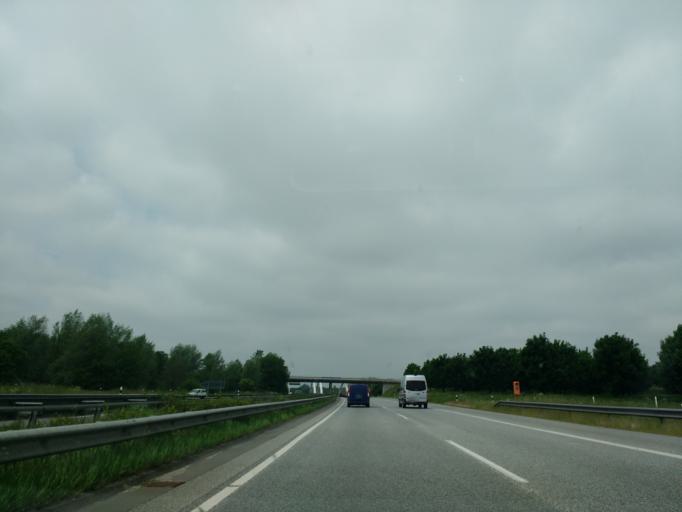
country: DE
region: Schleswig-Holstein
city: Krummesse
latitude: 53.8300
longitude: 10.6464
